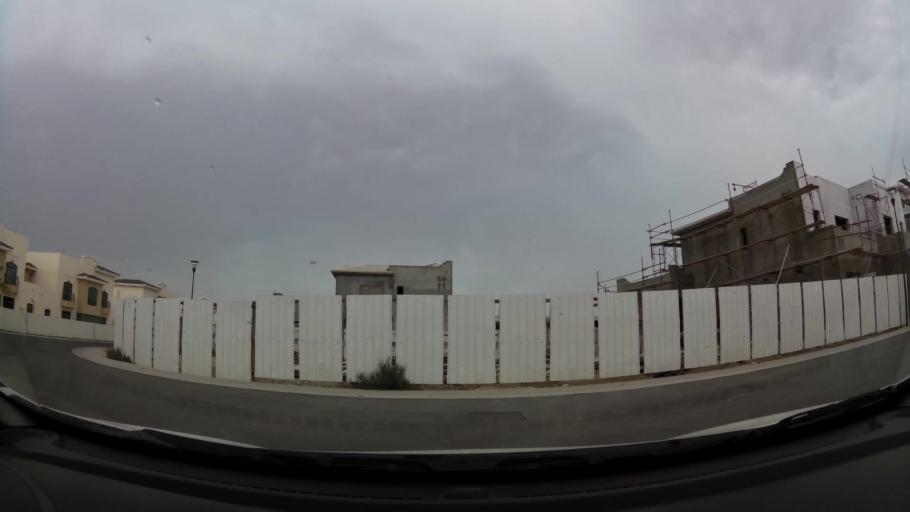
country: BH
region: Northern
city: Ar Rifa'
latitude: 26.0843
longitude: 50.5559
